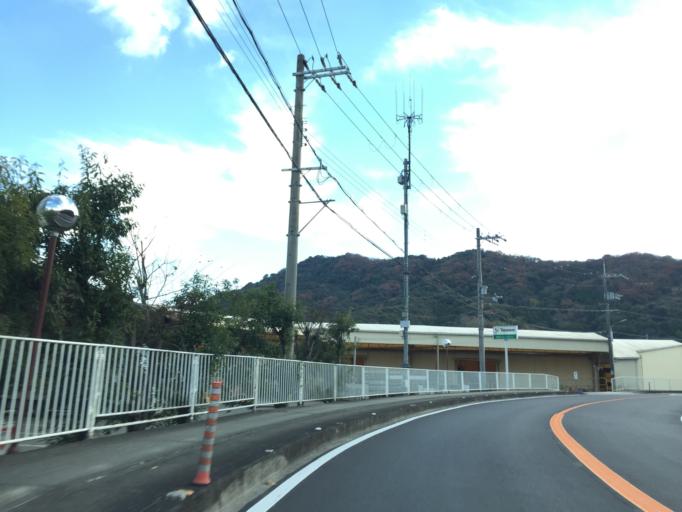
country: JP
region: Wakayama
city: Kainan
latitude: 34.1719
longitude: 135.2503
